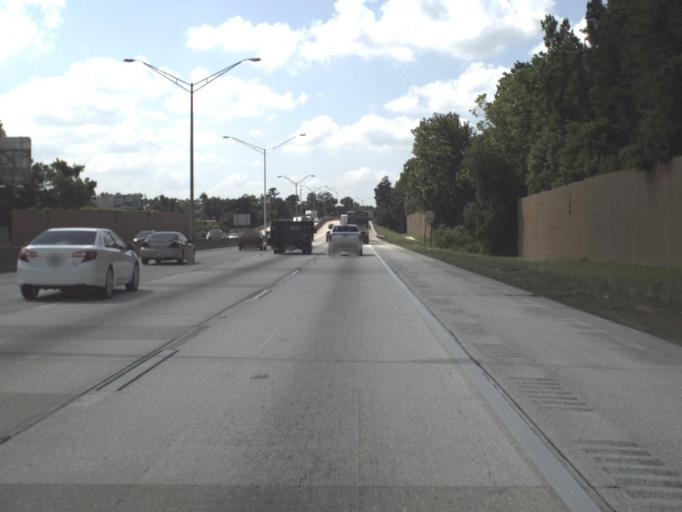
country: US
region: Florida
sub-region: Duval County
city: Jacksonville
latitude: 30.2969
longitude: -81.6363
